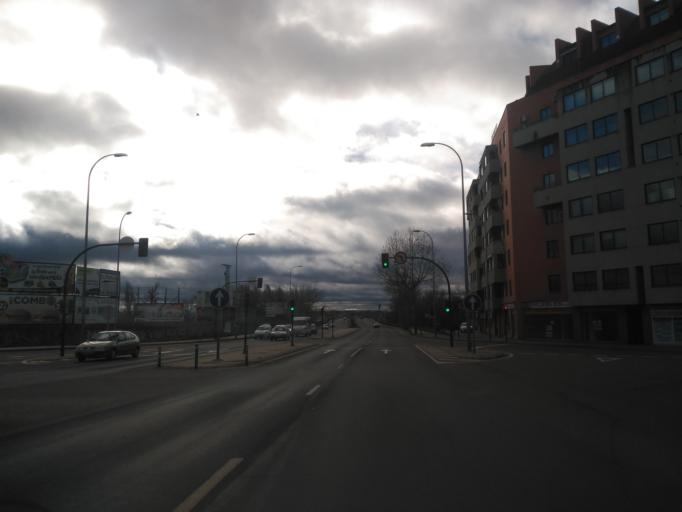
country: ES
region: Castille and Leon
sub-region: Provincia de Zamora
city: Zamora
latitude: 41.5055
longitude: -5.7322
